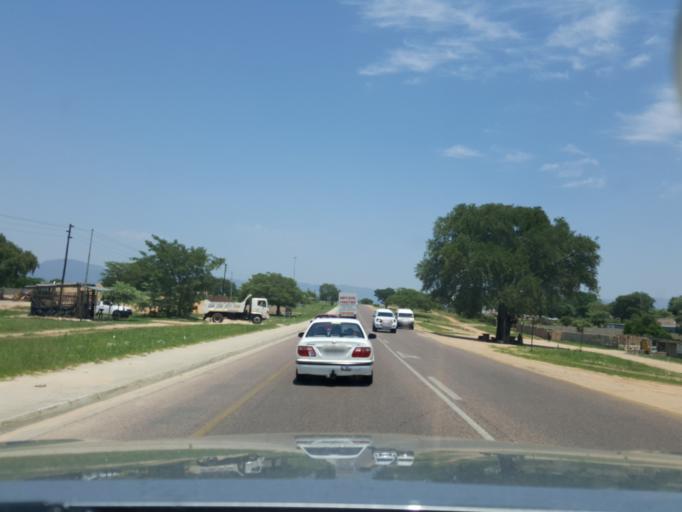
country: ZA
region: Limpopo
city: Thulamahashi
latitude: -24.7841
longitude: 31.0711
